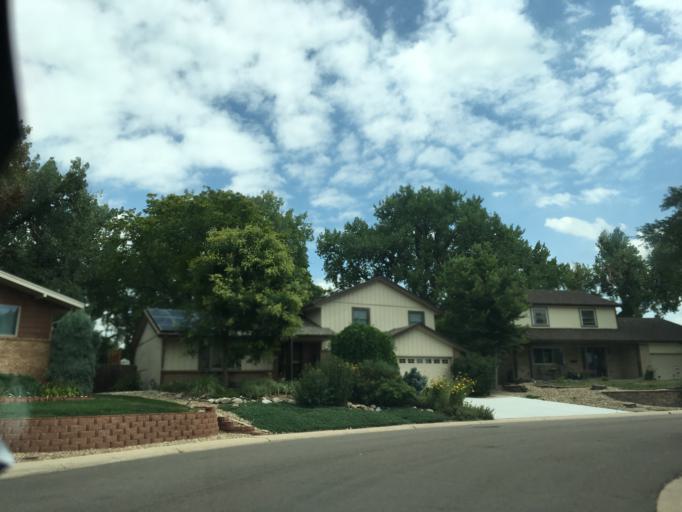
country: US
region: Colorado
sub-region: Arapahoe County
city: Sheridan
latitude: 39.6655
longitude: -105.0369
